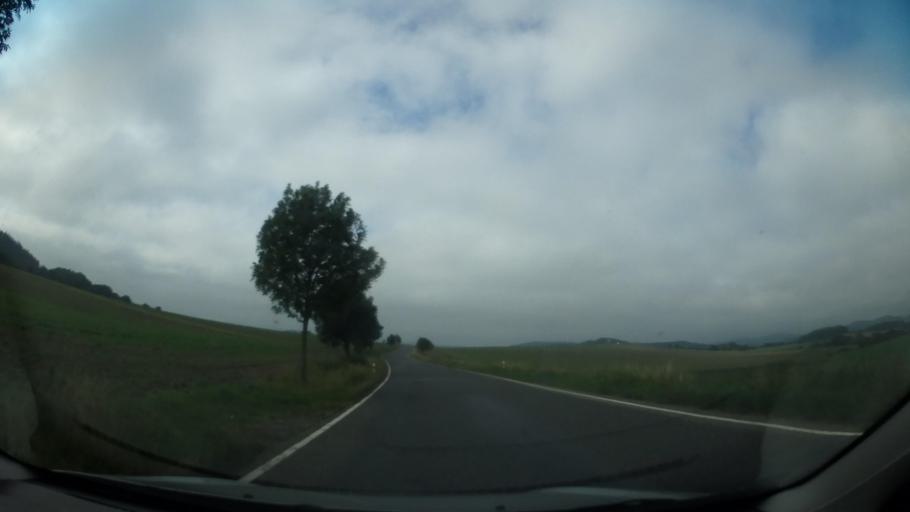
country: CZ
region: Central Bohemia
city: Sedlcany
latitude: 49.7056
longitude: 14.4484
